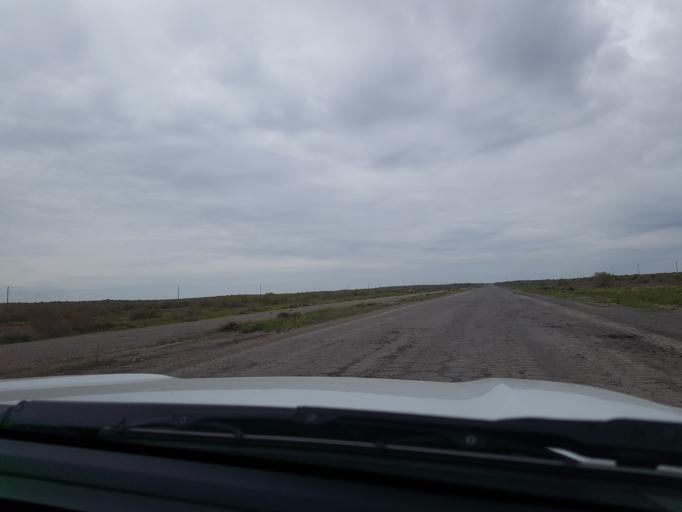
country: TM
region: Mary
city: Bayramaly
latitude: 37.9250
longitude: 62.6248
